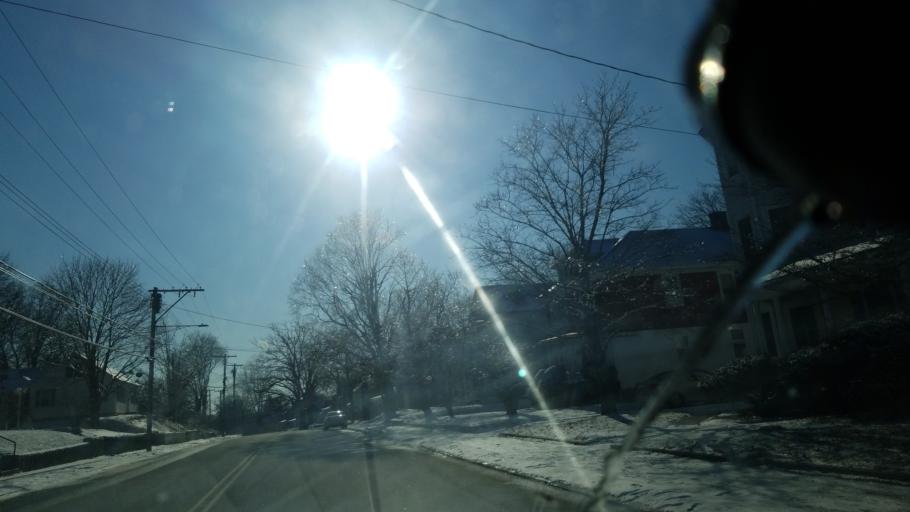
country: US
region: Connecticut
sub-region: Windham County
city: Danielson
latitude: 41.8023
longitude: -71.8803
